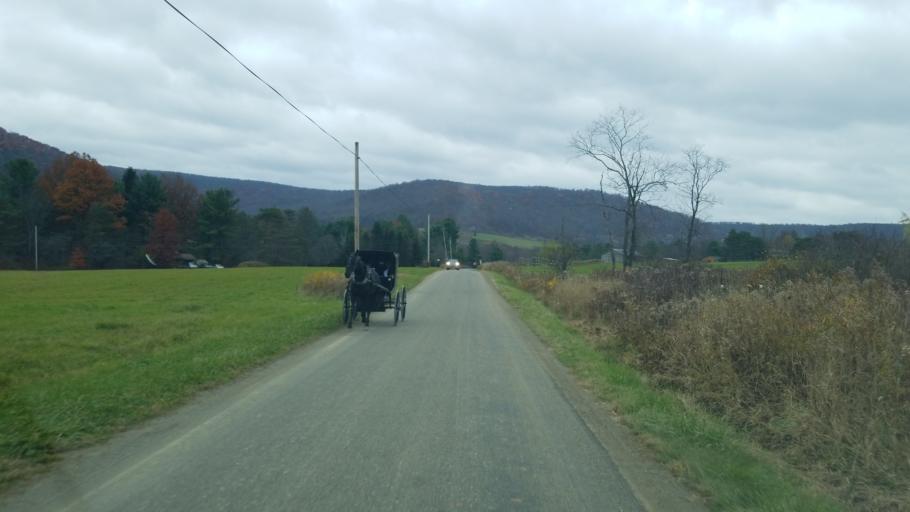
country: US
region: Pennsylvania
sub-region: McKean County
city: Smethport
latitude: 41.7806
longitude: -78.4226
